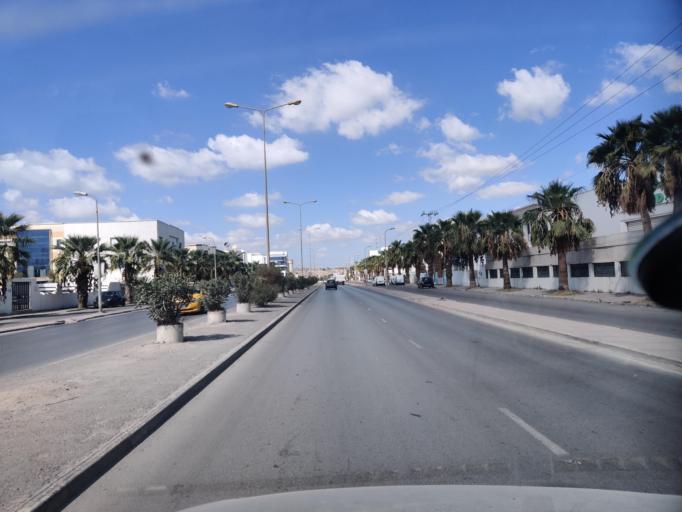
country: TN
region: Bin 'Arus
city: Ben Arous
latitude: 36.7745
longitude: 10.2181
